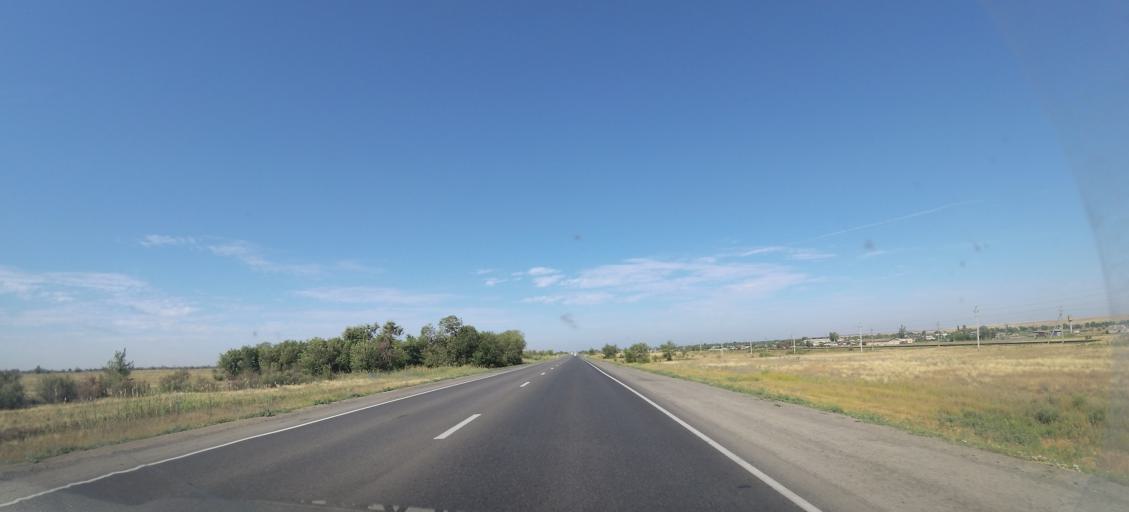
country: RU
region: Volgograd
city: Bereslavka
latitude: 48.6841
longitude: 43.9303
